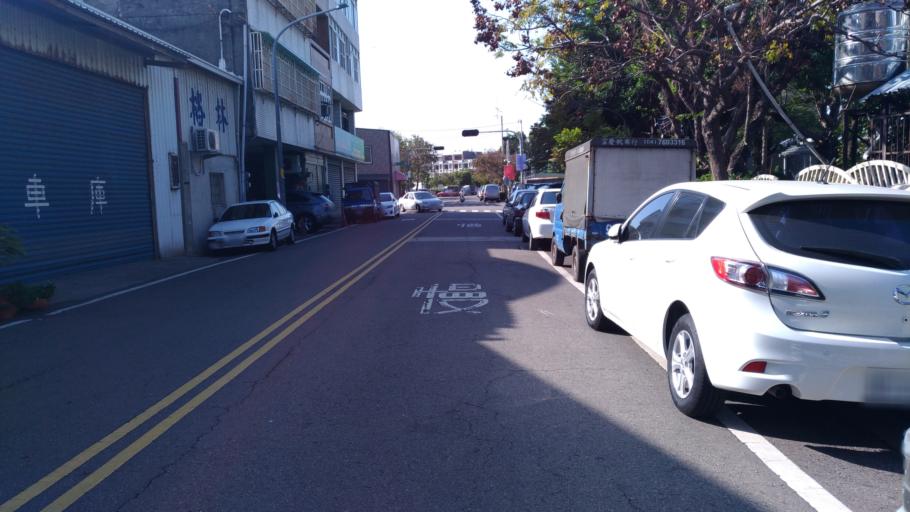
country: TW
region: Taiwan
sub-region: Changhua
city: Chang-hua
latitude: 24.0569
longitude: 120.4304
